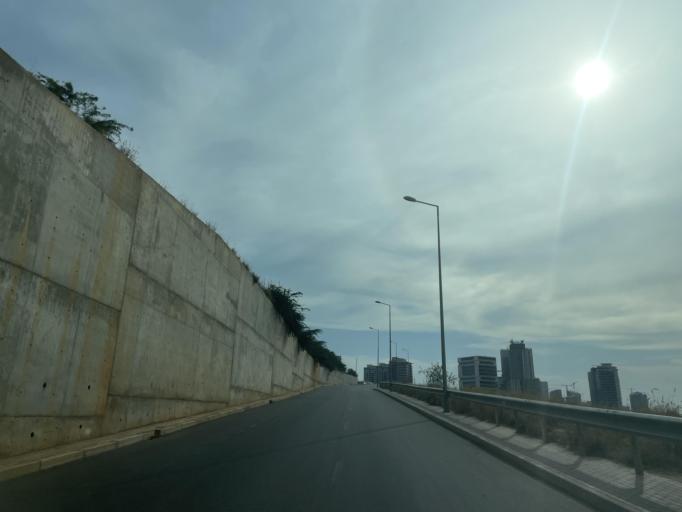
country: AO
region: Luanda
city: Luanda
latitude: -8.8062
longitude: 13.2477
